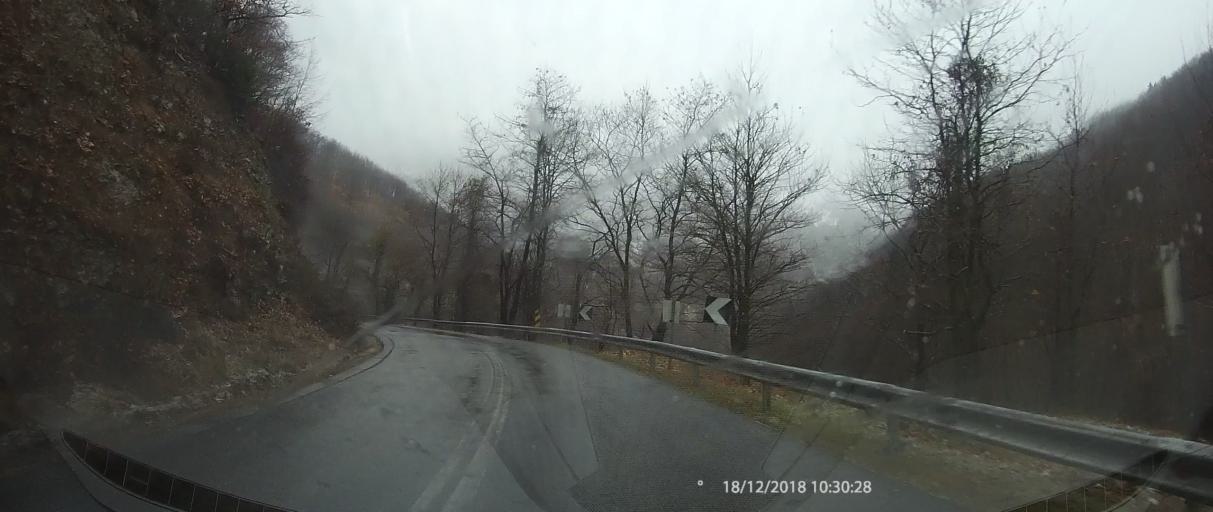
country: GR
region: Central Macedonia
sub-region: Nomos Pierias
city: Kato Milia
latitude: 40.1879
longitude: 22.2776
